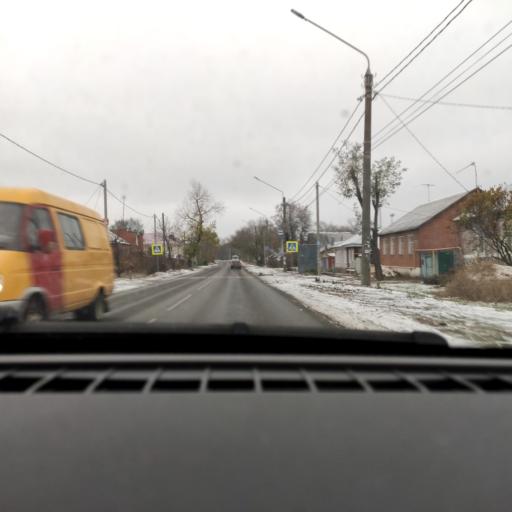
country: RU
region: Voronezj
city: Somovo
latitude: 51.7338
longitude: 39.2655
